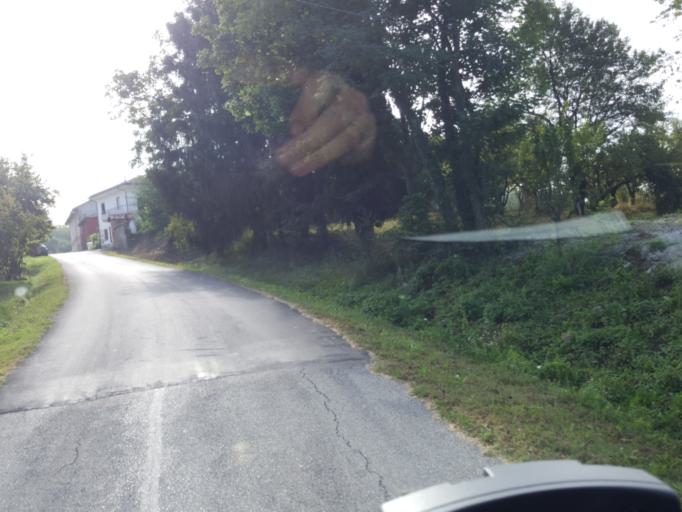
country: IT
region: Piedmont
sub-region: Provincia di Cuneo
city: Novello
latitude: 44.5954
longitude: 7.9104
